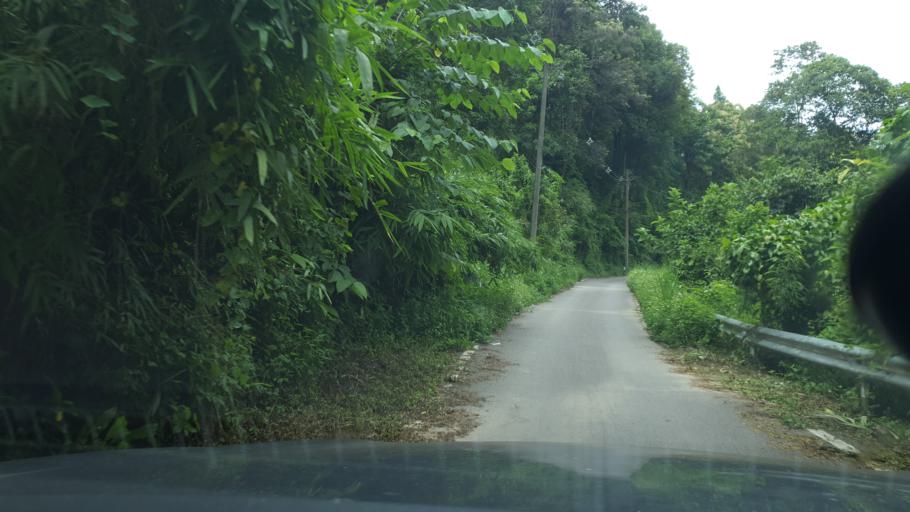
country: TH
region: Lamphun
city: Mae Tha
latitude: 18.5031
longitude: 99.2662
